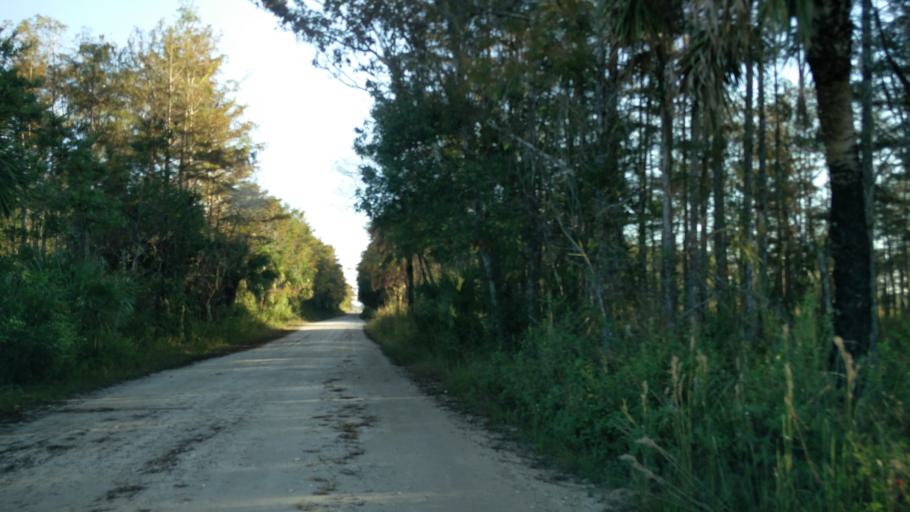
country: US
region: Florida
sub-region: Collier County
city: Lely Resort
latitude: 25.9763
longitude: -81.3697
